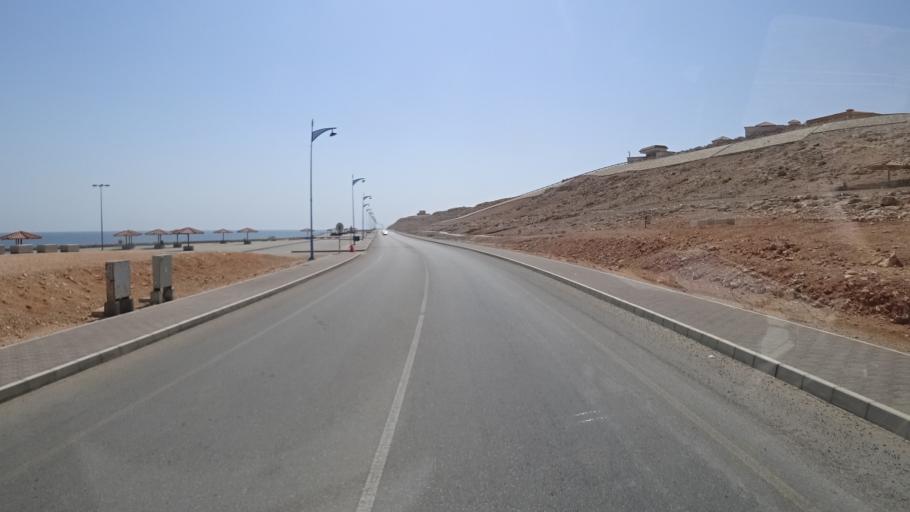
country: OM
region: Ash Sharqiyah
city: Sur
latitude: 22.5665
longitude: 59.5582
